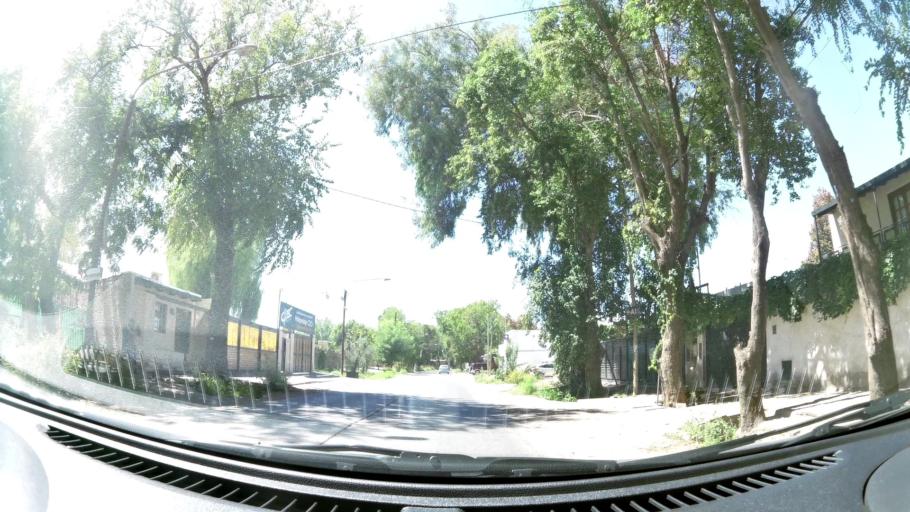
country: AR
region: Mendoza
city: Villa Nueva
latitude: -32.8682
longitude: -68.7894
